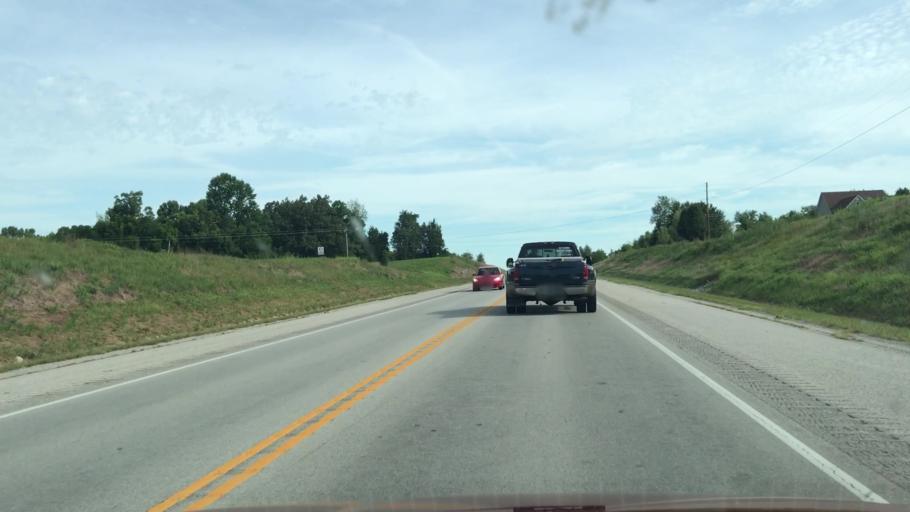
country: US
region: Kentucky
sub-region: Edmonson County
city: Brownsville
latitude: 37.1509
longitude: -86.2211
